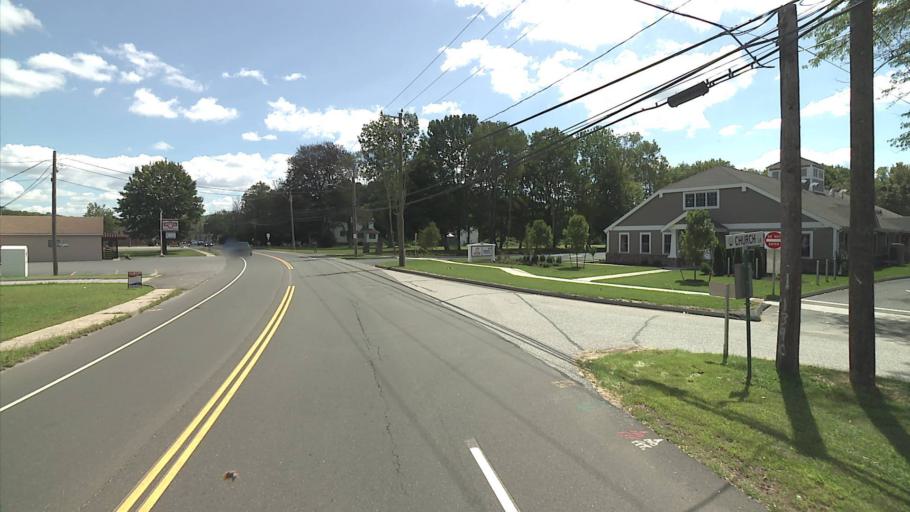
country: US
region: Connecticut
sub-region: New London County
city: Niantic
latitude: 41.3660
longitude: -72.2148
